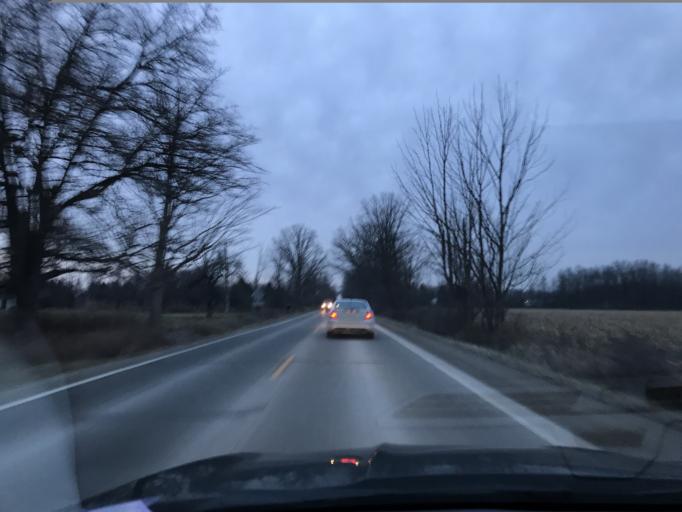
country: US
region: Michigan
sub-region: Macomb County
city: Romeo
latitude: 42.8340
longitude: -82.9638
